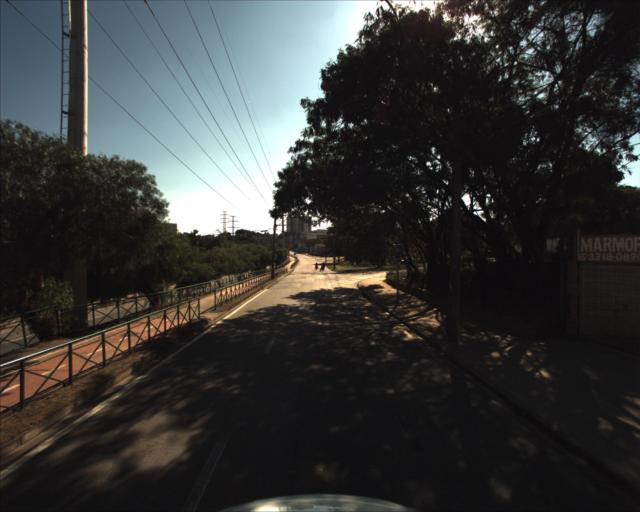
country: BR
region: Sao Paulo
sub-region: Sorocaba
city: Sorocaba
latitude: -23.4547
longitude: -47.4793
